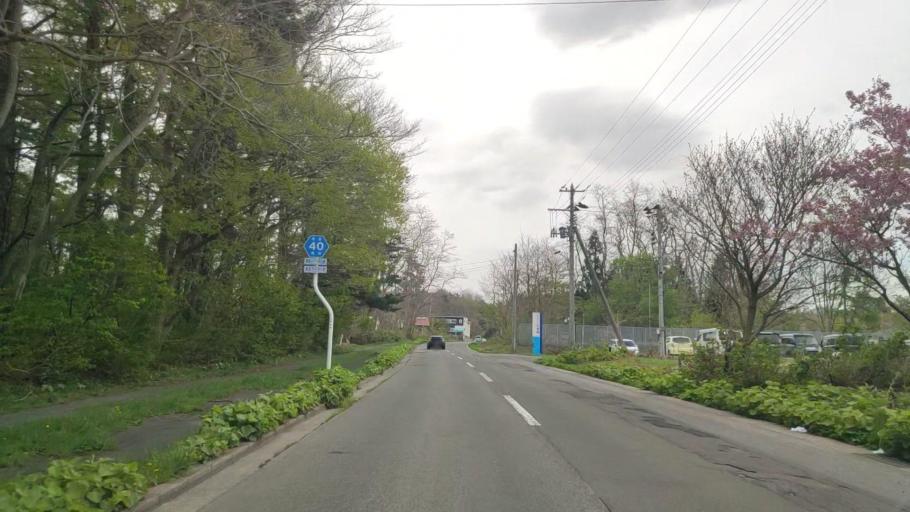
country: JP
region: Aomori
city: Aomori Shi
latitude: 40.7678
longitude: 140.8007
